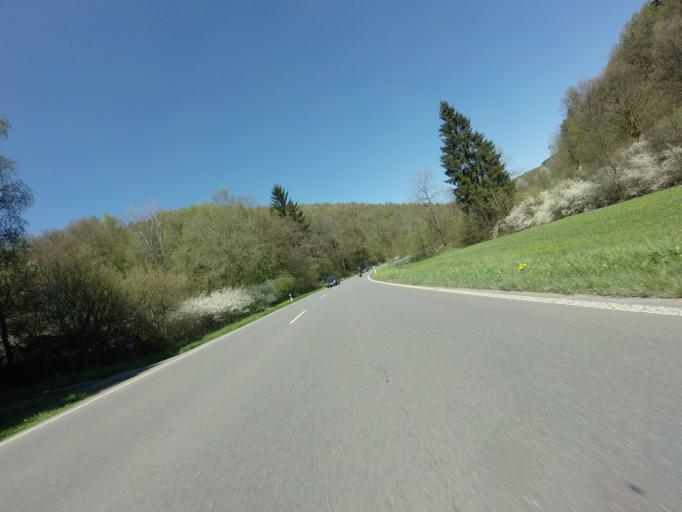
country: DE
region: North Rhine-Westphalia
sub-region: Regierungsbezirk Arnsberg
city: Olpe
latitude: 51.0278
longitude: 7.8932
